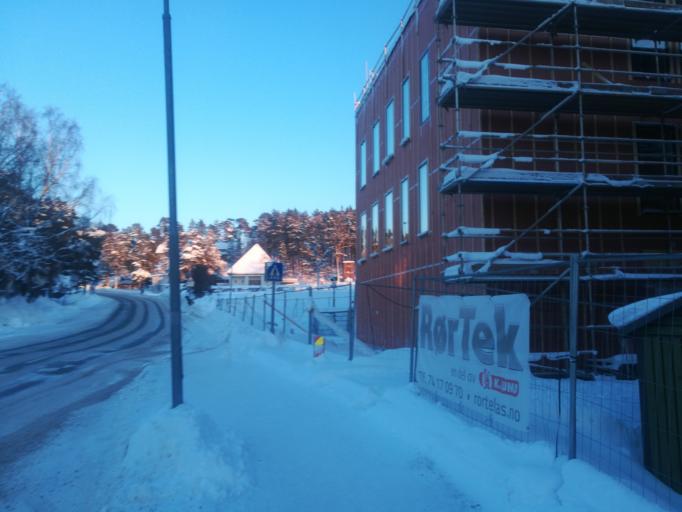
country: NO
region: Nord-Trondelag
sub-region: Steinkjer
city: Steinkjer
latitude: 64.0138
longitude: 11.4999
